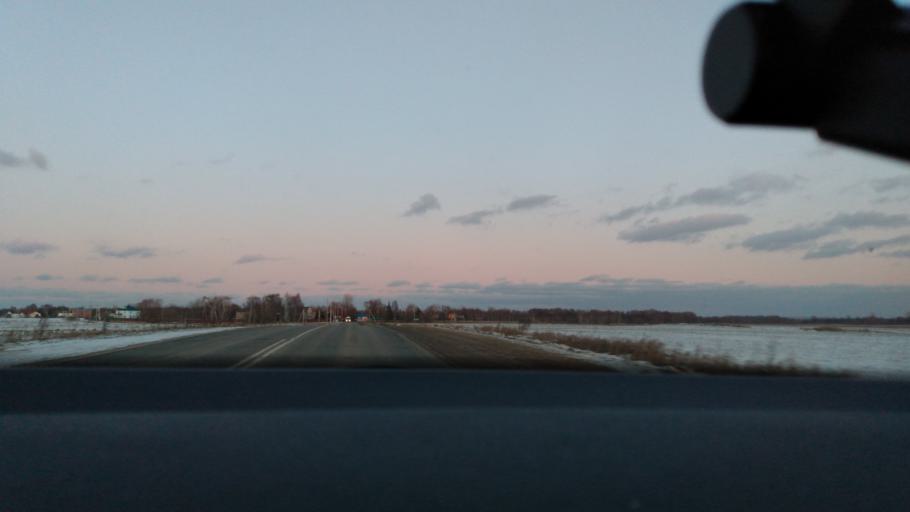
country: RU
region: Moskovskaya
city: Krasnaya Poyma
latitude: 55.1095
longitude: 39.0207
